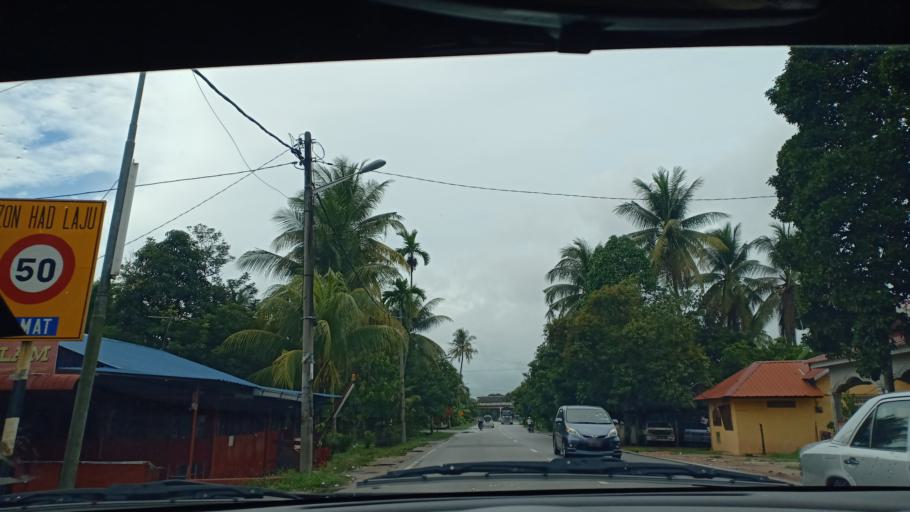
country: MY
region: Penang
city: Kepala Batas
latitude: 5.4972
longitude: 100.4387
